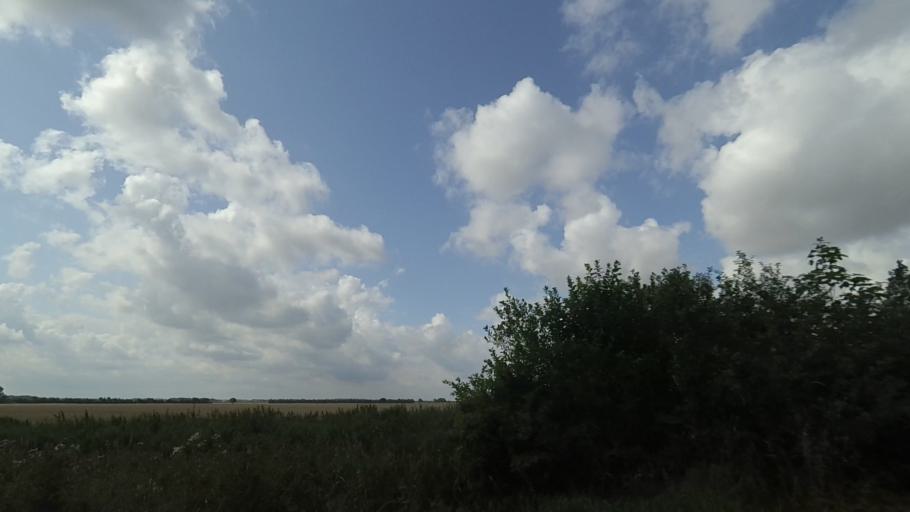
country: DK
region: Central Jutland
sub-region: Norddjurs Kommune
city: Auning
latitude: 56.5099
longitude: 10.4193
